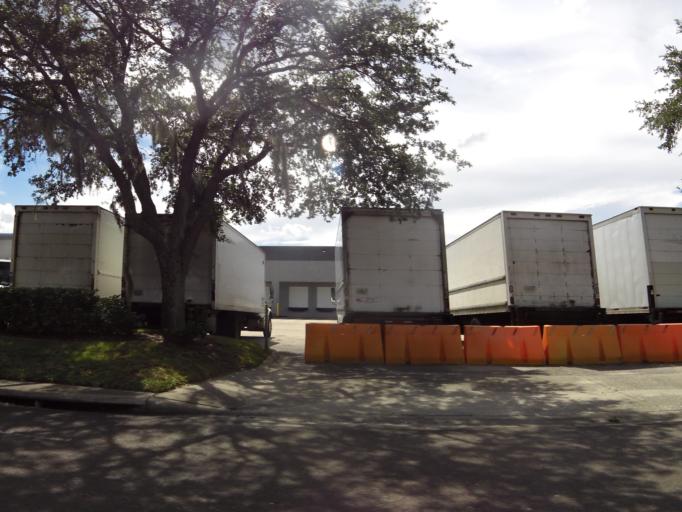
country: US
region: Florida
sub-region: Duval County
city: Jacksonville
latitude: 30.4246
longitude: -81.6359
